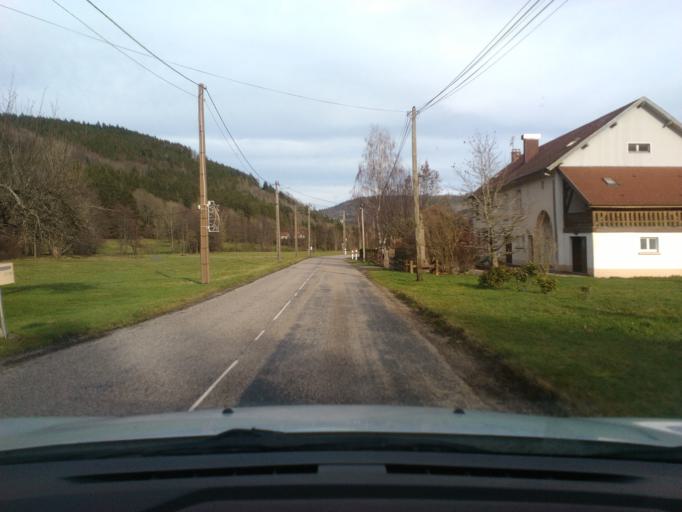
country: FR
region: Lorraine
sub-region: Departement des Vosges
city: Anould
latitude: 48.1392
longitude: 6.9674
